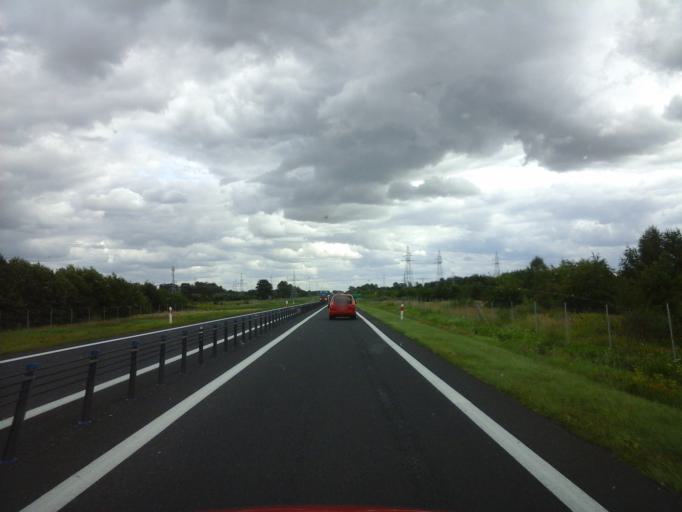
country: PL
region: West Pomeranian Voivodeship
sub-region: Powiat stargardzki
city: Kobylanka
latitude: 53.3615
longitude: 14.9052
